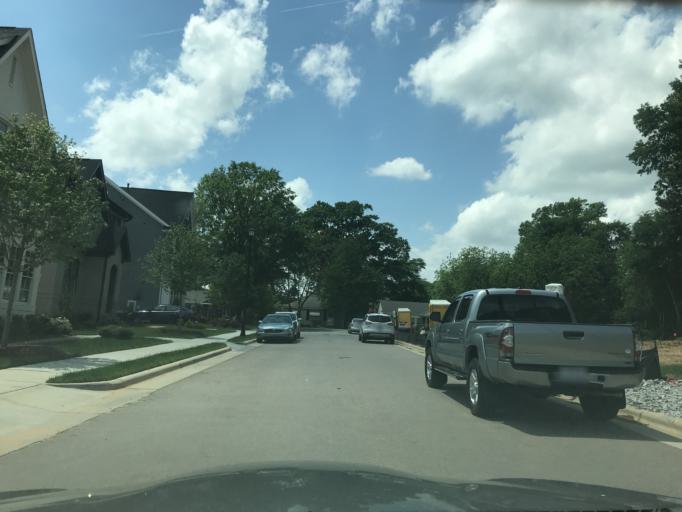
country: US
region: North Carolina
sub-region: Wake County
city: Raleigh
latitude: 35.7923
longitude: -78.6292
